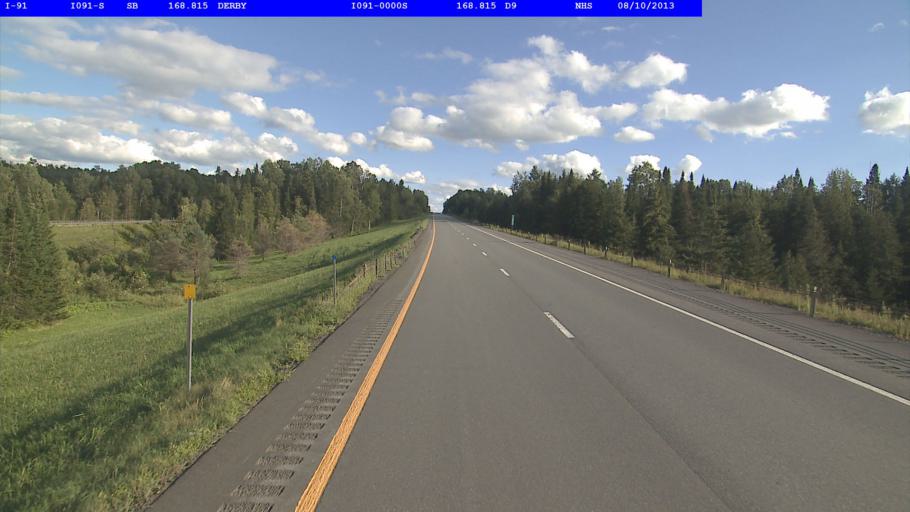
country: US
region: Vermont
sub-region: Orleans County
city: Newport
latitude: 44.9055
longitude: -72.1785
